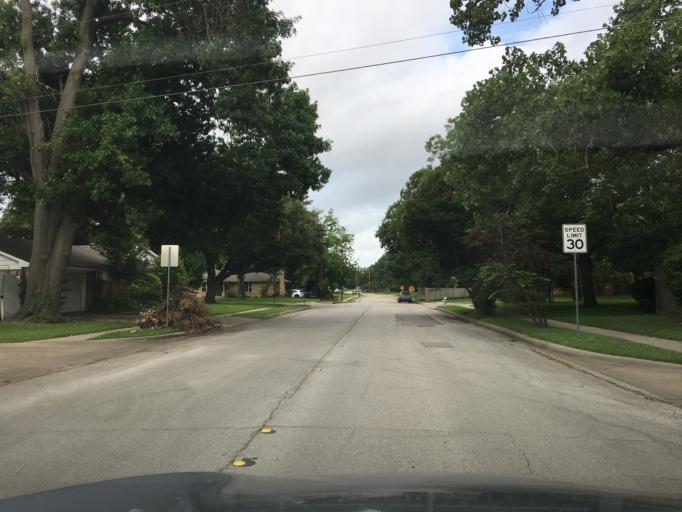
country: US
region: Texas
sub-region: Dallas County
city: Richardson
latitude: 32.9455
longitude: -96.7217
